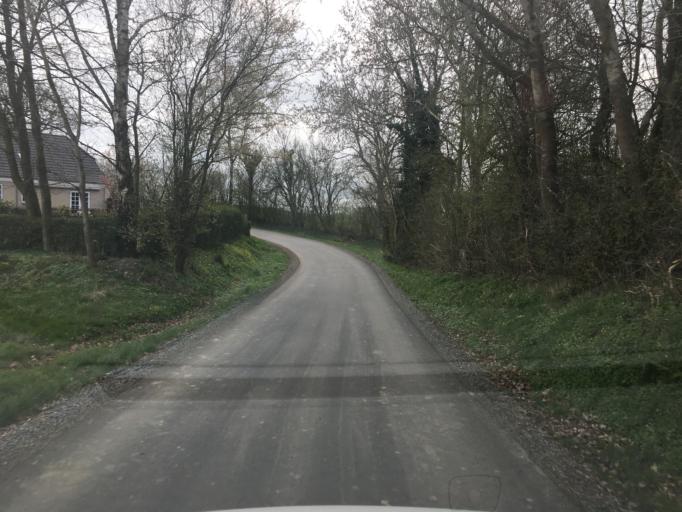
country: DE
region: Schleswig-Holstein
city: Glucksburg
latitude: 54.9008
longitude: 9.5266
